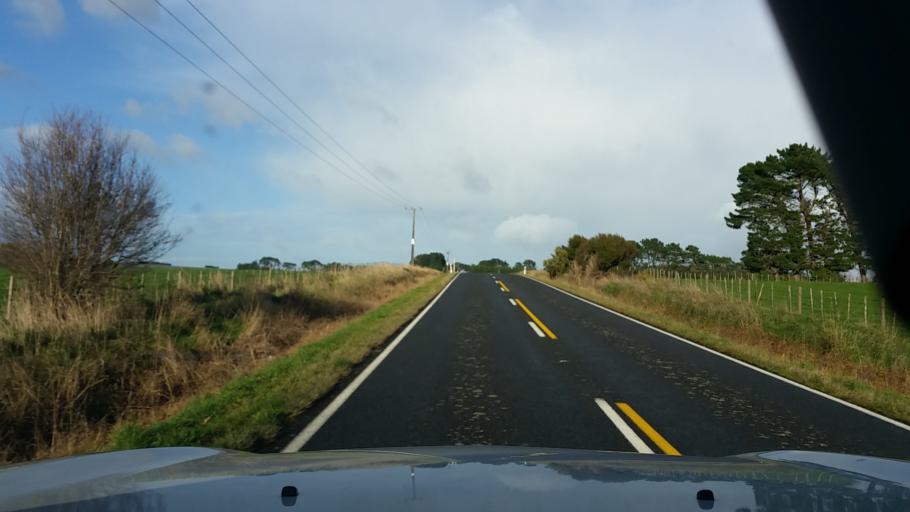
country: NZ
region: Wellington
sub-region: Upper Hutt City
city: Upper Hutt
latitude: -41.3574
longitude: 175.2018
